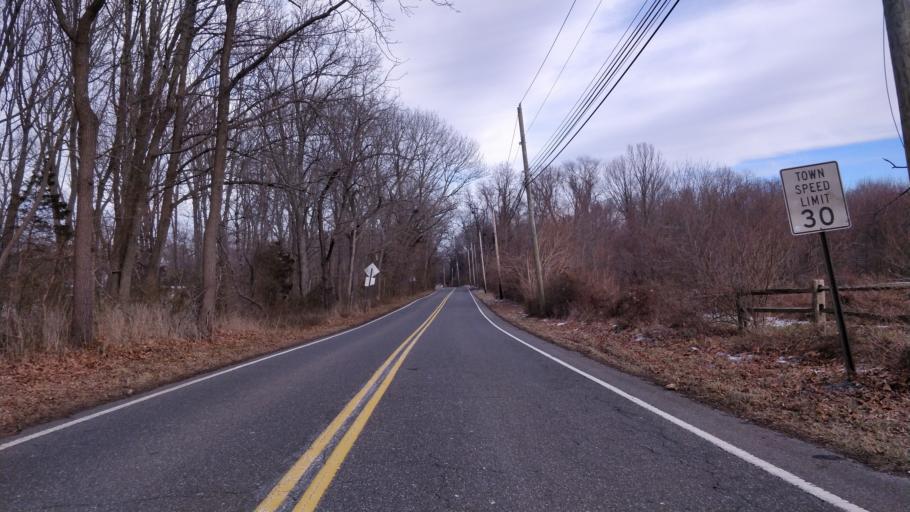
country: US
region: New York
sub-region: Suffolk County
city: Cold Spring Harbor
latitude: 40.8601
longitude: -73.4546
